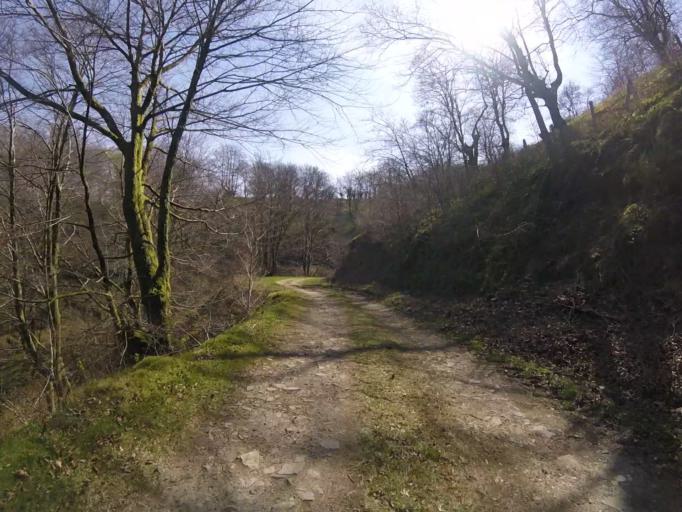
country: ES
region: Basque Country
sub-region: Provincia de Guipuzcoa
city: Irun
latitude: 43.2527
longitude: -1.8129
